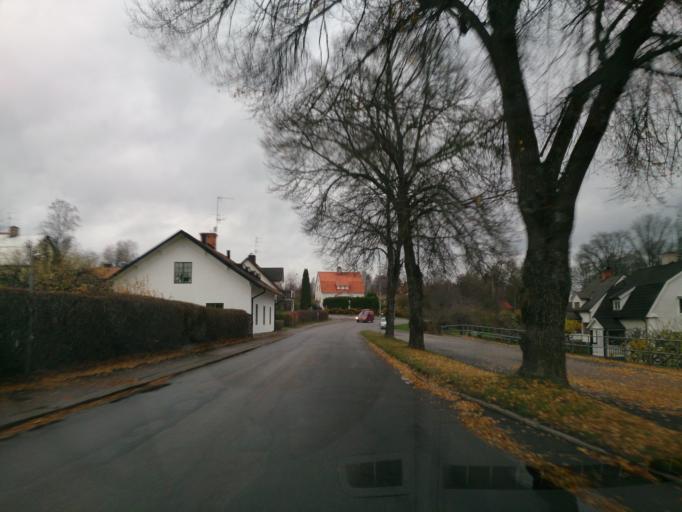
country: SE
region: OEstergoetland
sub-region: Atvidabergs Kommun
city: Atvidaberg
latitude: 58.2044
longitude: 15.9916
